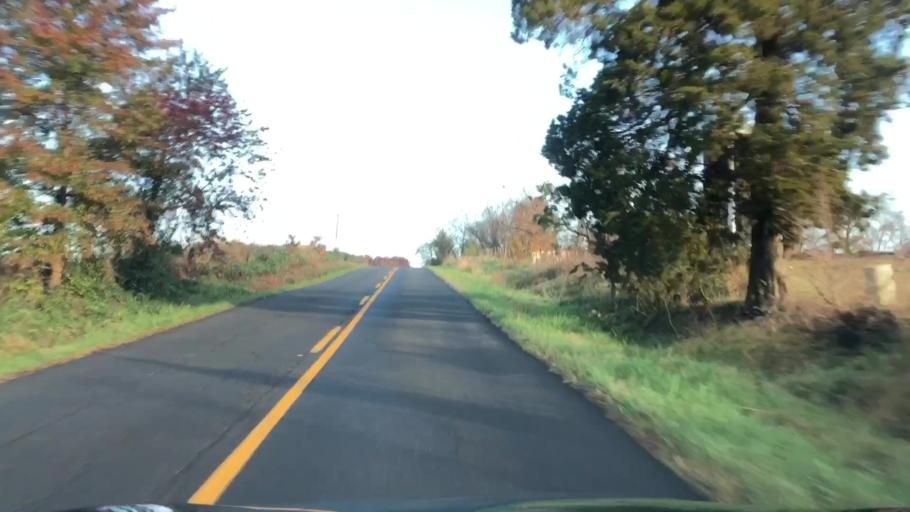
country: US
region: Virginia
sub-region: Prince William County
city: Nokesville
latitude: 38.6823
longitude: -77.6671
